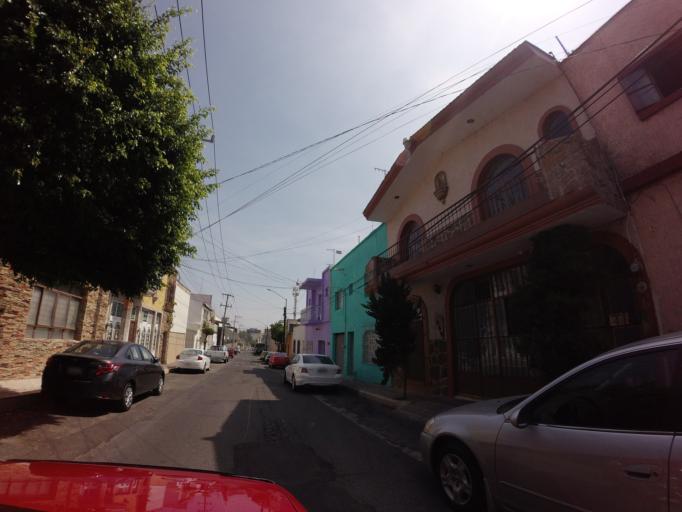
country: MX
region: Jalisco
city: Guadalajara
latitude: 20.6900
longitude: -103.3471
